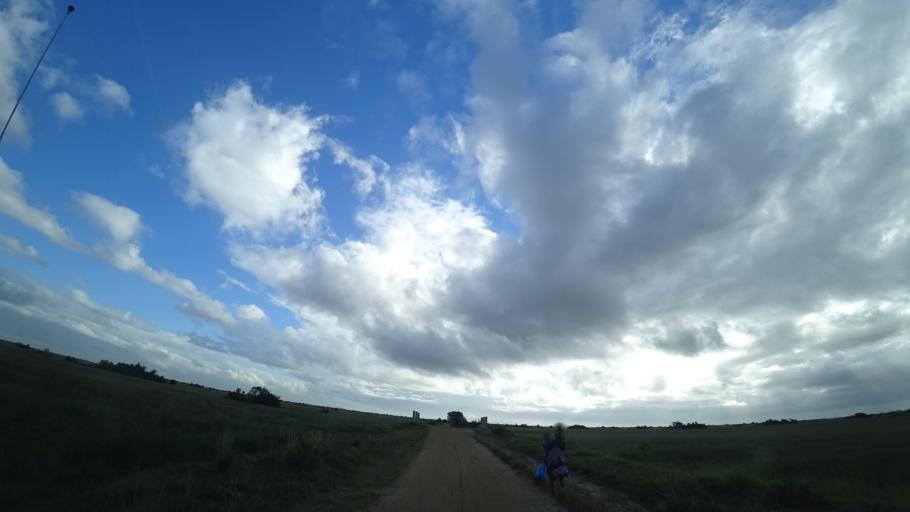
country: MZ
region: Sofala
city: Beira
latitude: -19.7099
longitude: 35.0169
